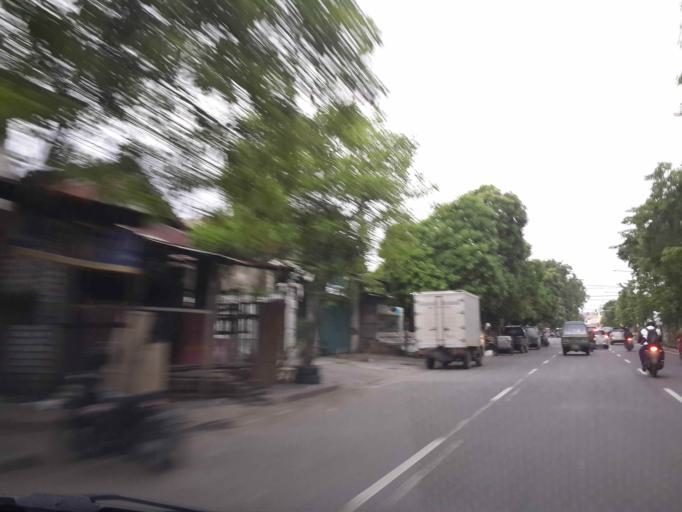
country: ID
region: East Java
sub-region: Kota Surabaya
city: Surabaya
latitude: -7.2525
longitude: 112.7206
